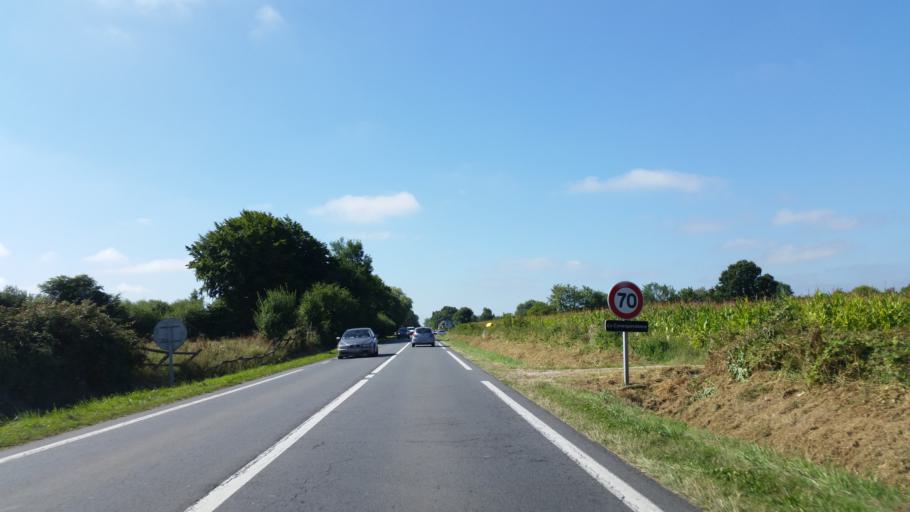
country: FR
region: Lower Normandy
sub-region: Departement du Calvados
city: Saint-Gatien-des-Bois
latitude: 49.3658
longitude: 0.2024
